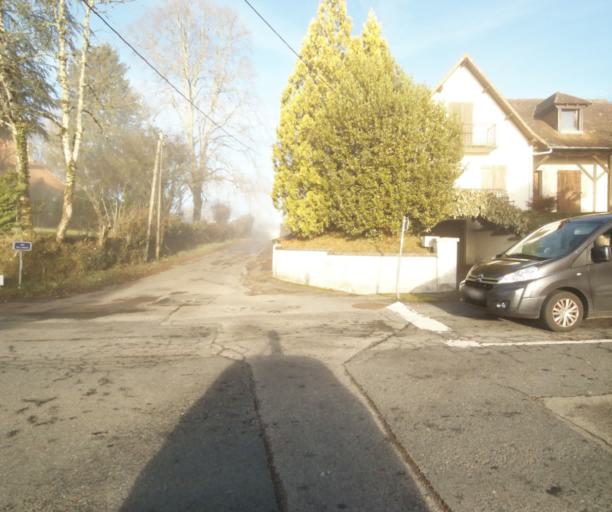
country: FR
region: Limousin
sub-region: Departement de la Correze
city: Tulle
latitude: 45.2645
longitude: 1.7798
